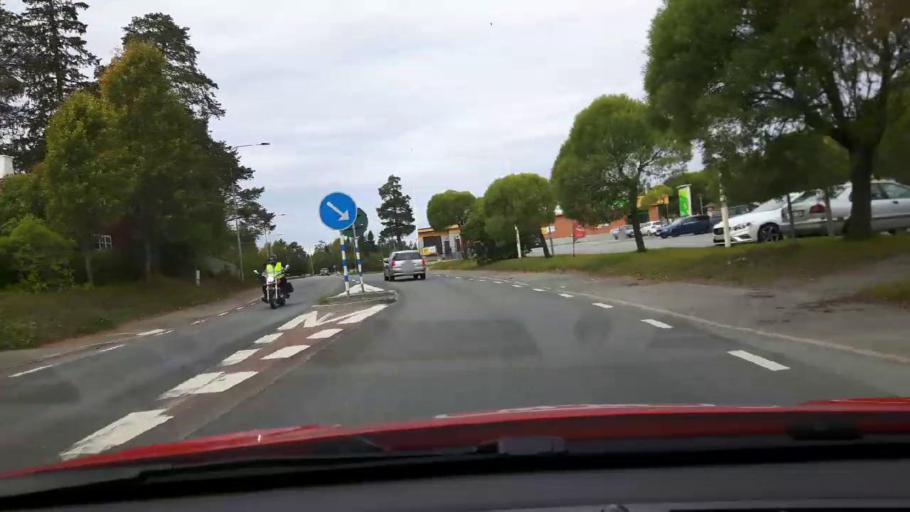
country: SE
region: Jaemtland
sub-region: OEstersunds Kommun
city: Brunflo
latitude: 63.0801
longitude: 14.8262
